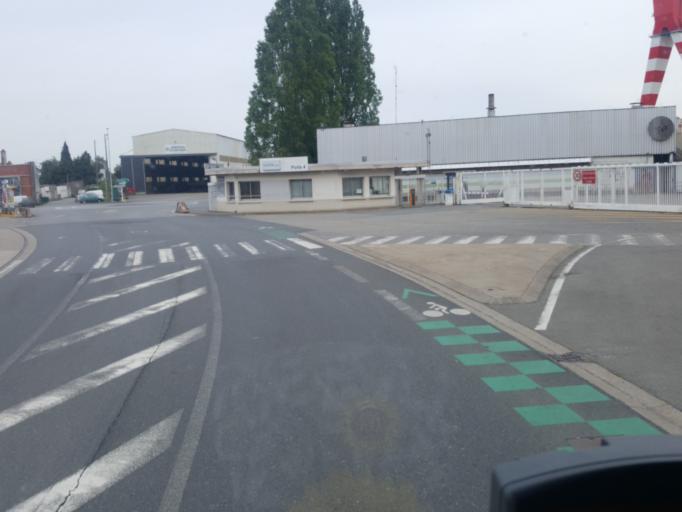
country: FR
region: Pays de la Loire
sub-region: Departement de la Loire-Atlantique
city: Saint-Nazaire
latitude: 47.2889
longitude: -2.1921
